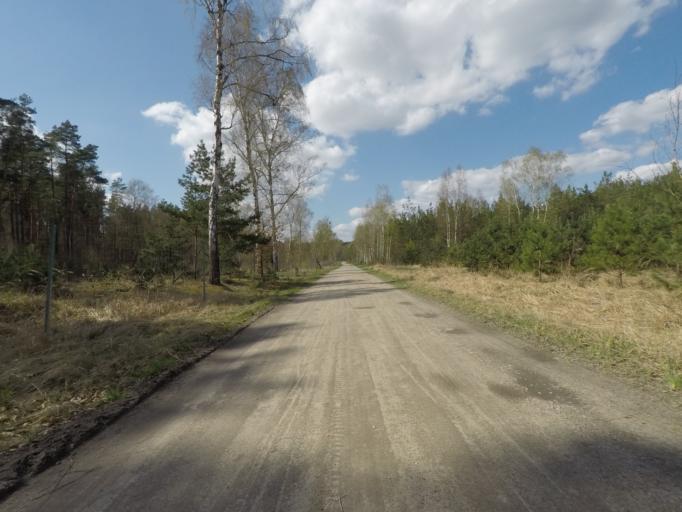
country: DE
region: Brandenburg
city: Marienwerder
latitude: 52.8280
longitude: 13.6617
